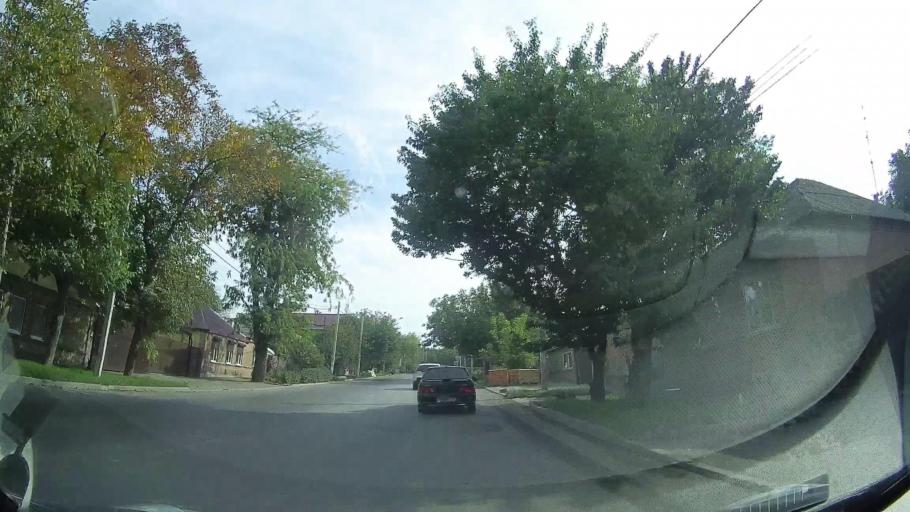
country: RU
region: Rostov
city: Severnyy
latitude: 47.2688
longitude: 39.7072
